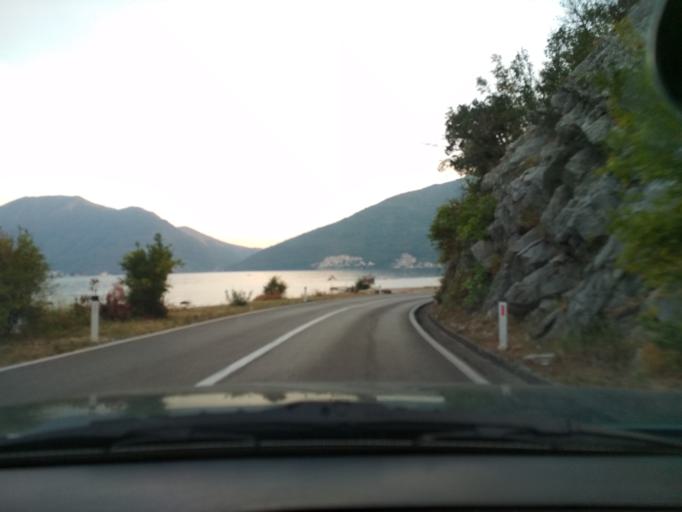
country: ME
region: Kotor
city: Risan
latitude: 42.5064
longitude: 18.6768
